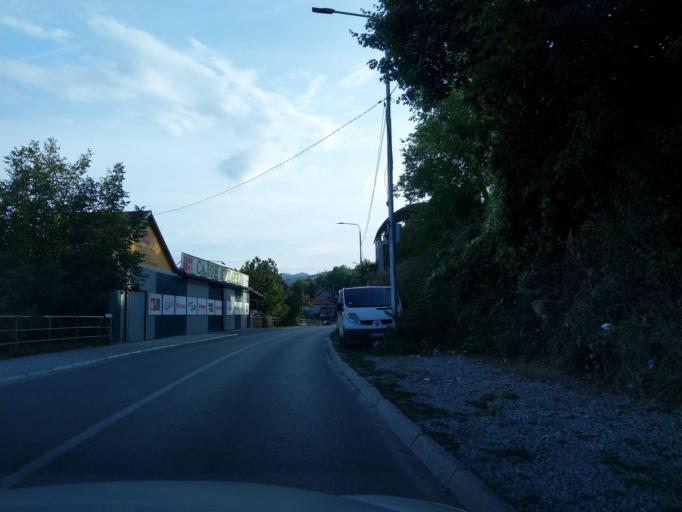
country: RS
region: Central Serbia
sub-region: Zlatiborski Okrug
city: Prijepolje
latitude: 43.3563
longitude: 19.6356
